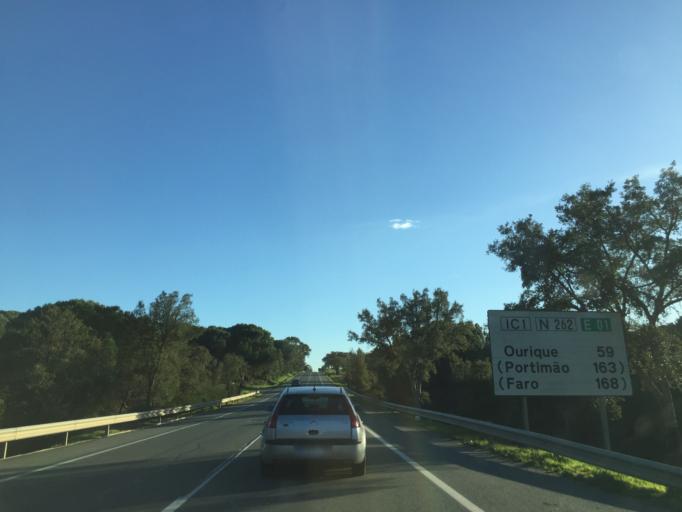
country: PT
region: Setubal
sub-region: Grandola
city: Grandola
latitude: 38.1080
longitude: -8.4183
